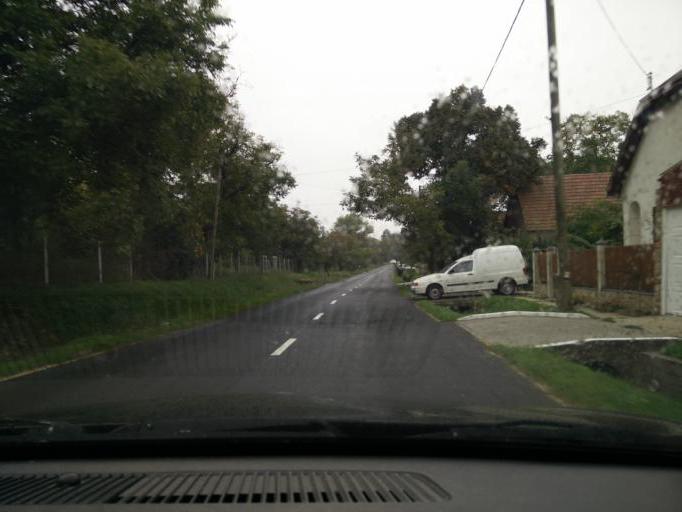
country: HU
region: Pest
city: Perbal
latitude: 47.6262
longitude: 18.7789
